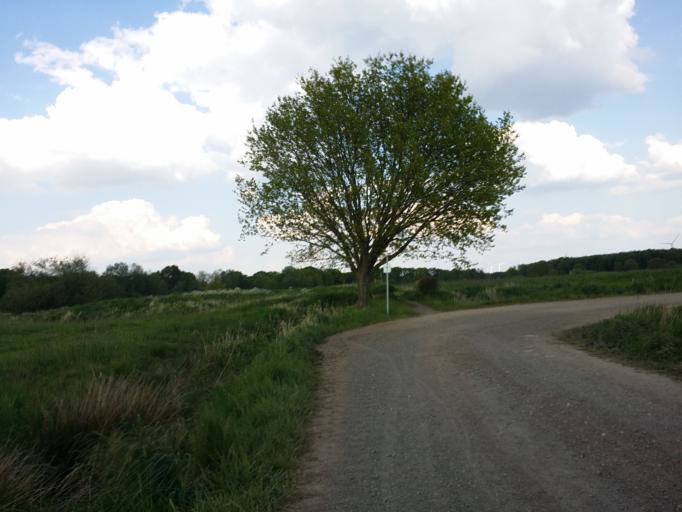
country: DE
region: Lower Saxony
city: Loxstedt
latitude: 53.4479
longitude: 8.6541
